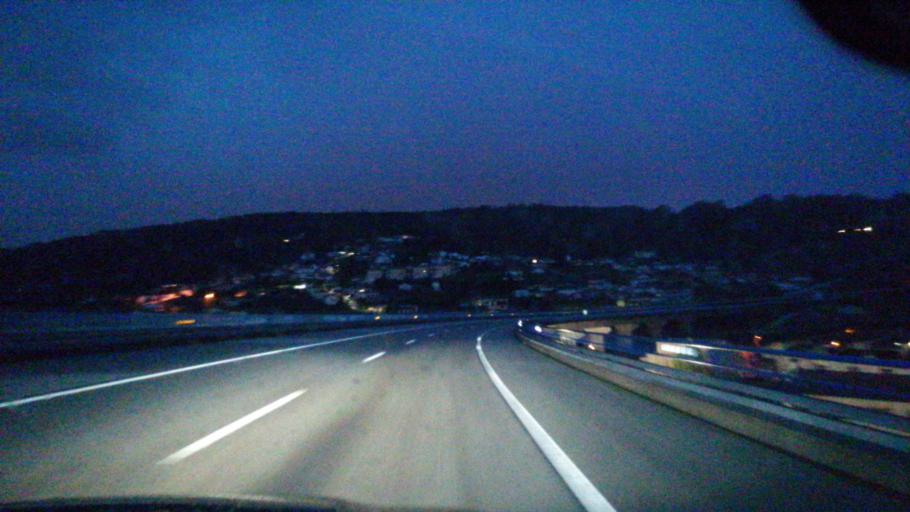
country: PT
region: Braga
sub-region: Guimaraes
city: Candoso
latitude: 41.4090
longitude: -8.3185
